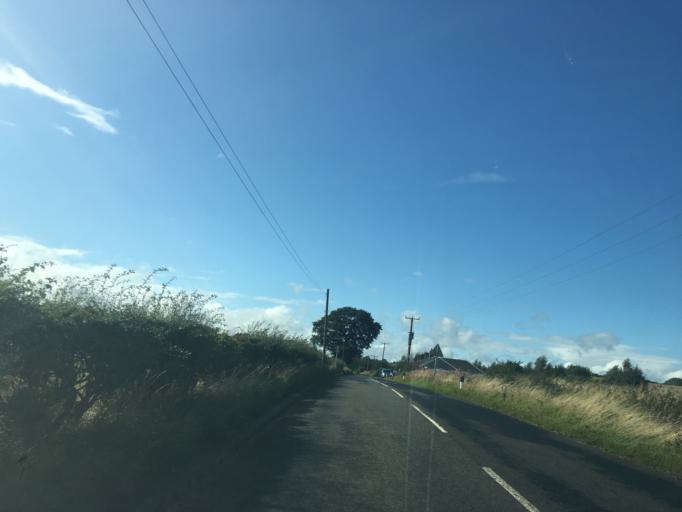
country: GB
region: Scotland
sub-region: Edinburgh
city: Kirkliston
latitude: 55.9658
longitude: -3.3675
